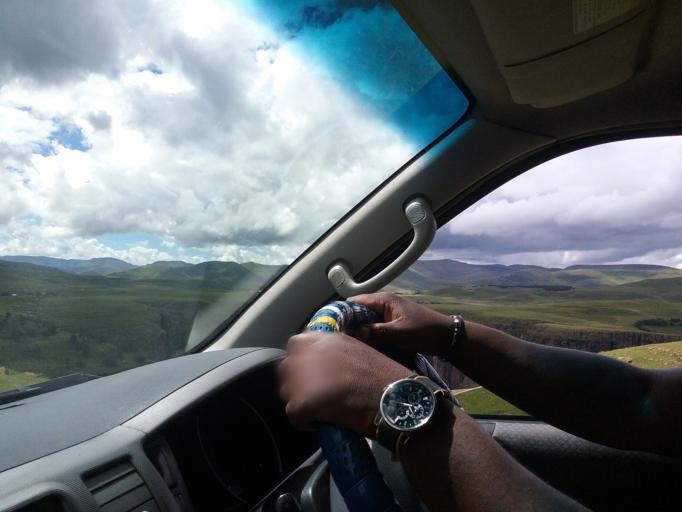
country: LS
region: Maseru
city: Nako
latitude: -29.8781
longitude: 28.0479
